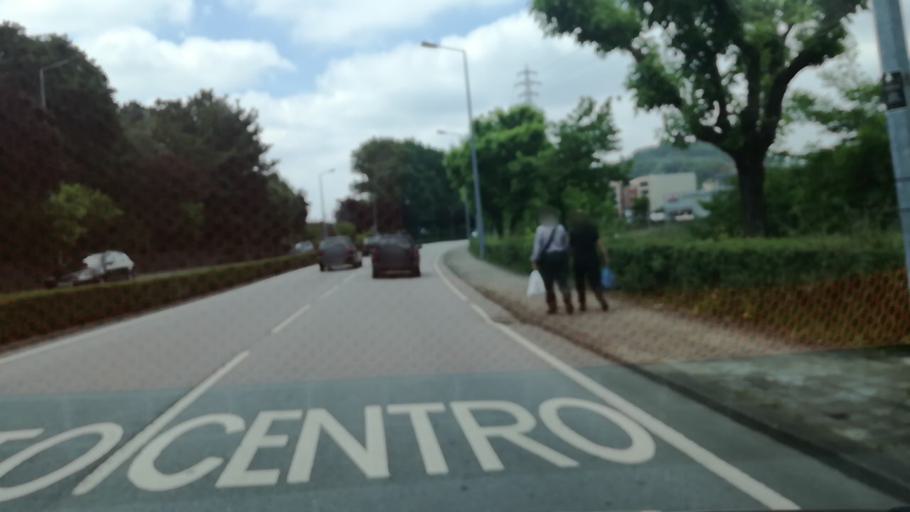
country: PT
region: Braga
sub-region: Vila Nova de Famalicao
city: Vila Nova de Famalicao
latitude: 41.3971
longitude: -8.5184
